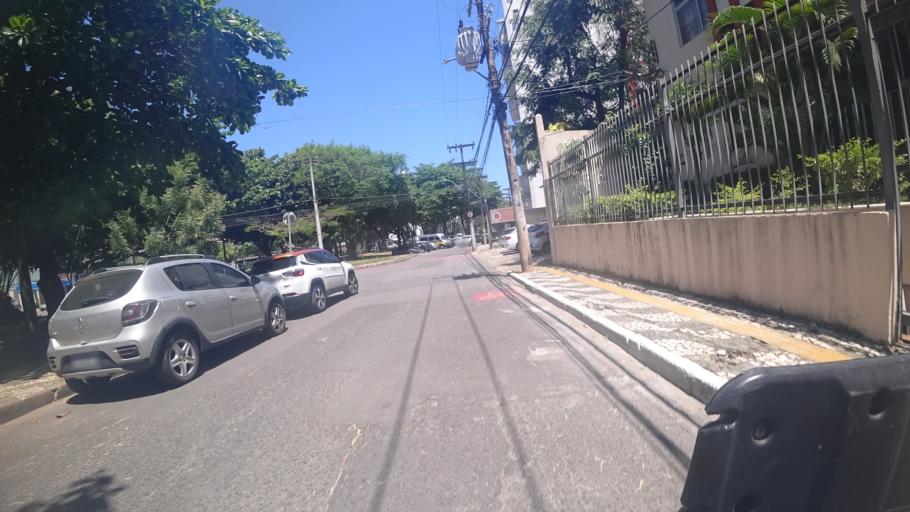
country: BR
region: Bahia
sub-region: Salvador
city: Salvador
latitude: -12.9867
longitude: -38.4586
